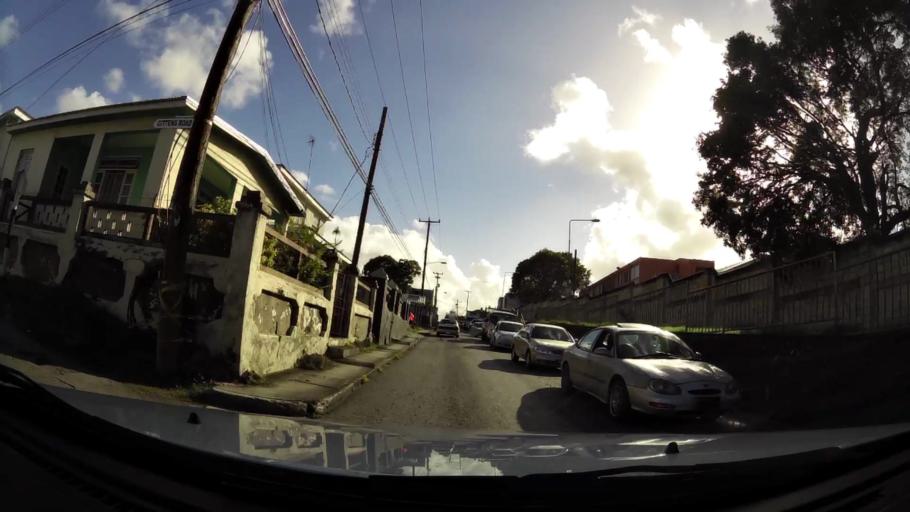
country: BB
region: Saint Michael
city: Bridgetown
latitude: 13.1020
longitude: -59.5964
